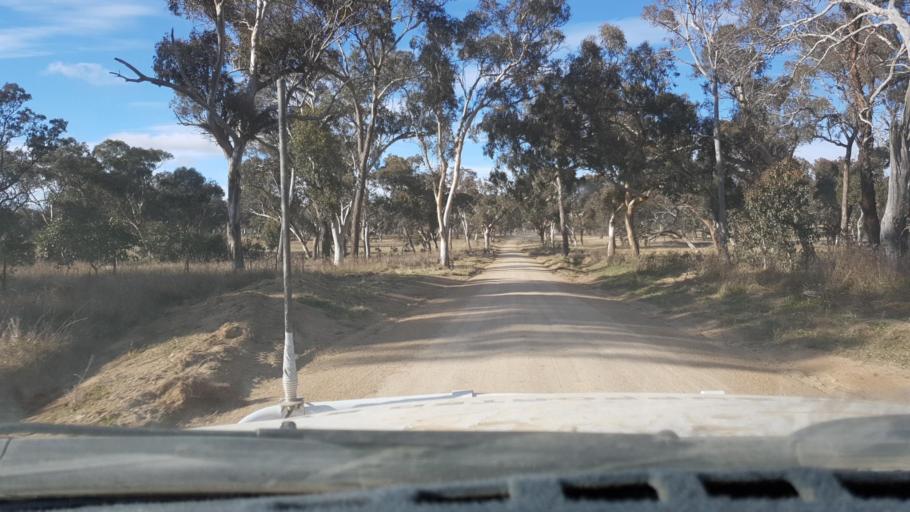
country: AU
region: New South Wales
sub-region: Armidale Dumaresq
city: Enmore
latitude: -30.7217
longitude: 151.5911
